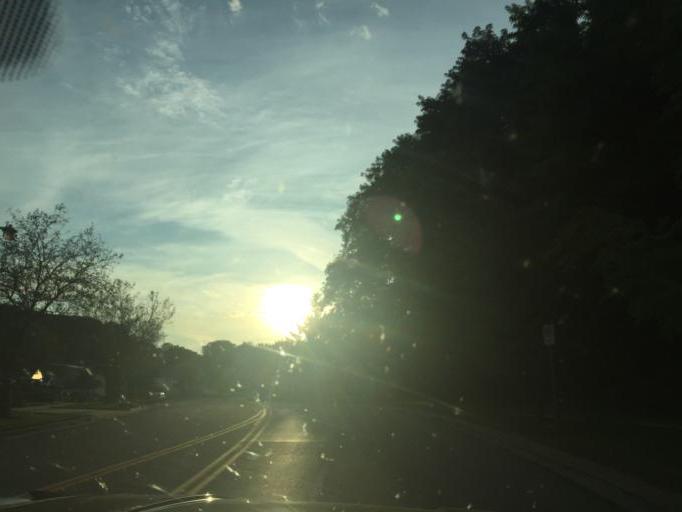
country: US
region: Minnesota
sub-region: Olmsted County
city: Rochester
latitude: 44.0054
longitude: -92.4872
